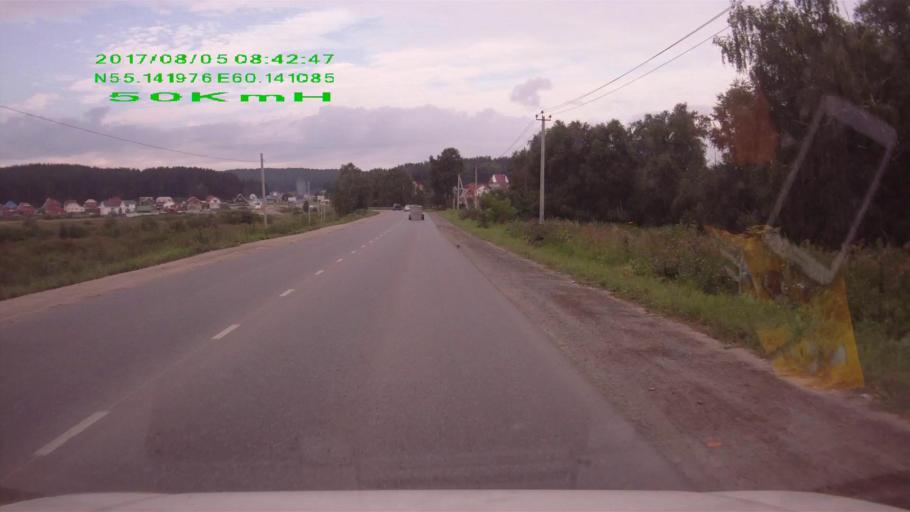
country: RU
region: Chelyabinsk
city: Turgoyak
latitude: 55.1420
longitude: 60.1409
